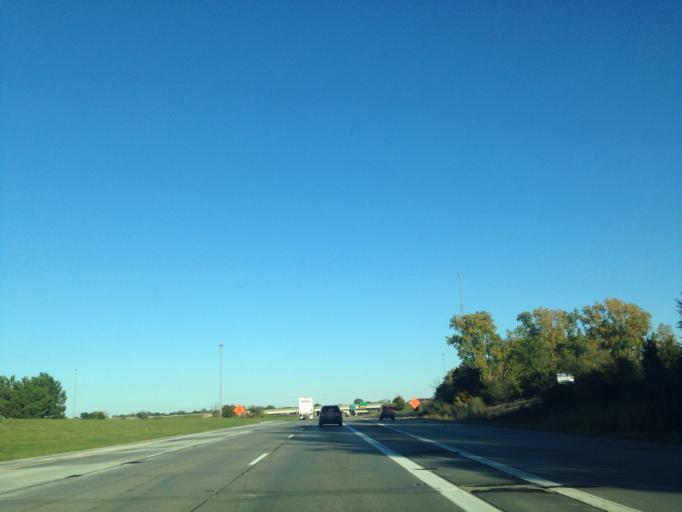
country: US
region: Michigan
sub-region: Wayne County
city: Plymouth
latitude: 42.3866
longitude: -83.4434
